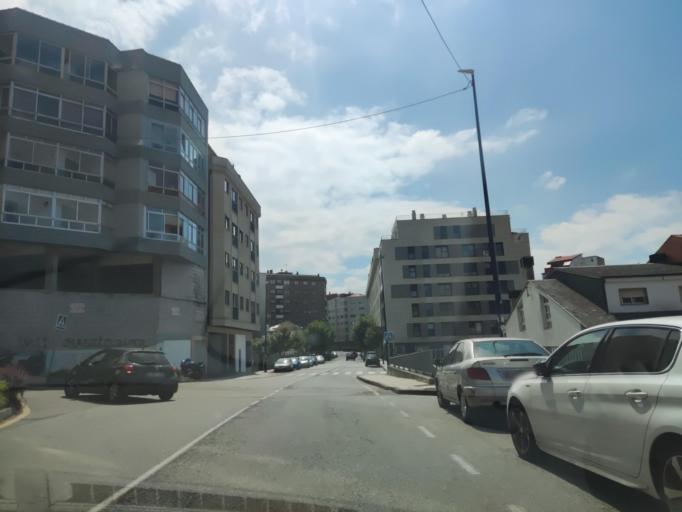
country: ES
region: Galicia
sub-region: Provincia de Pontevedra
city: Vigo
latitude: 42.2502
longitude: -8.6983
